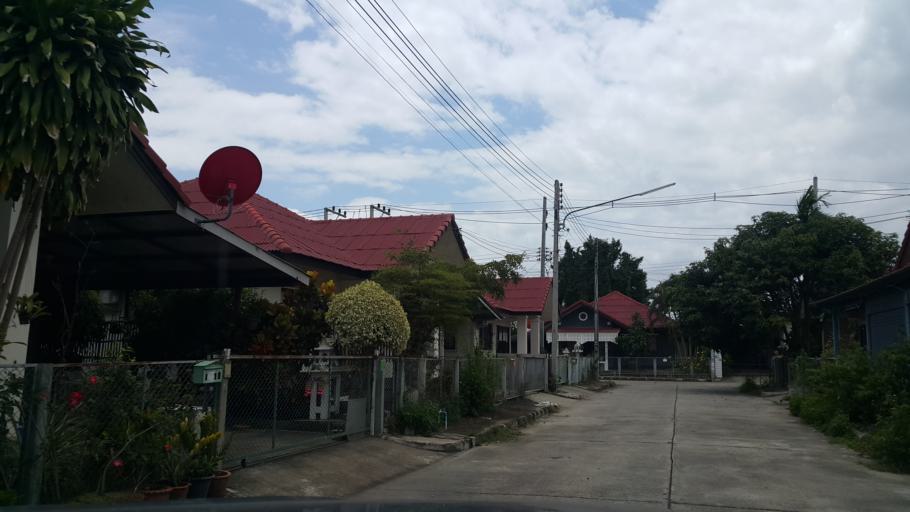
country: TH
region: Chiang Mai
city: Hang Dong
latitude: 18.7076
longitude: 98.9691
